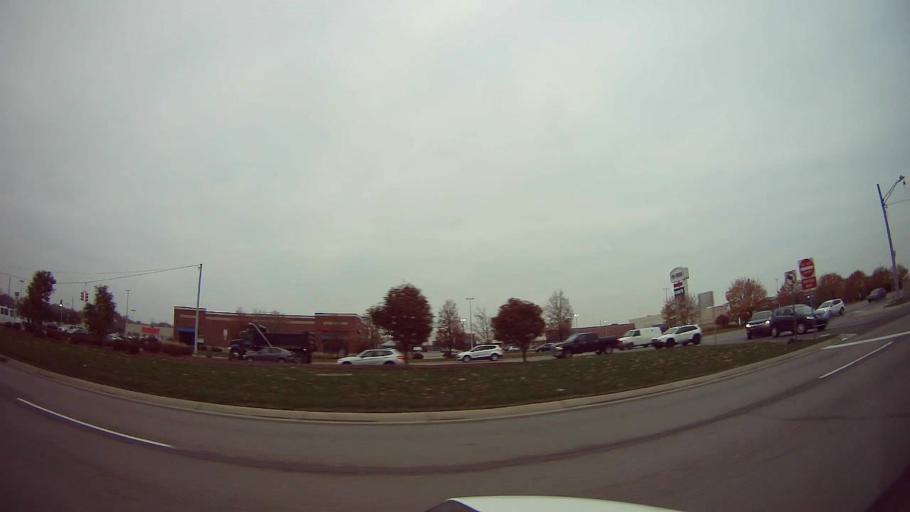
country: US
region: Michigan
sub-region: Oakland County
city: Bingham Farms
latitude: 42.4989
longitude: -83.2854
